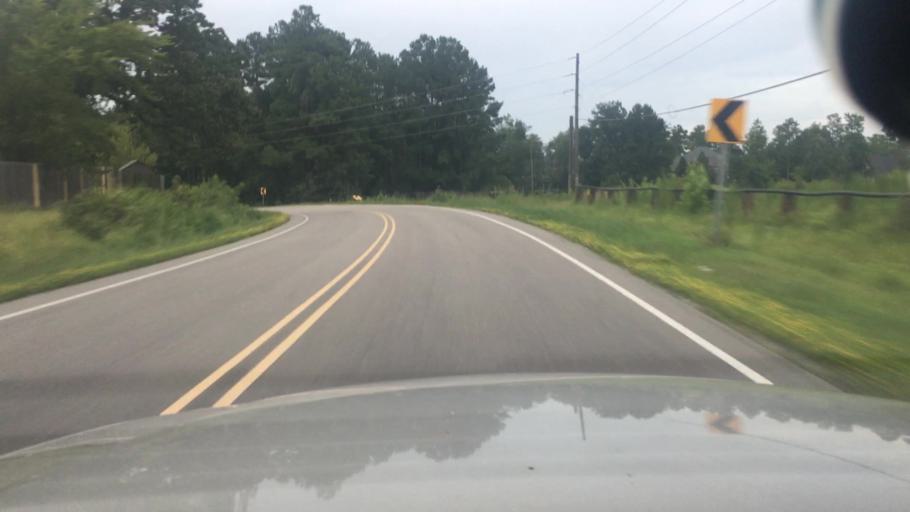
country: US
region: North Carolina
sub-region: Hoke County
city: Rockfish
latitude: 34.9976
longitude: -79.0235
